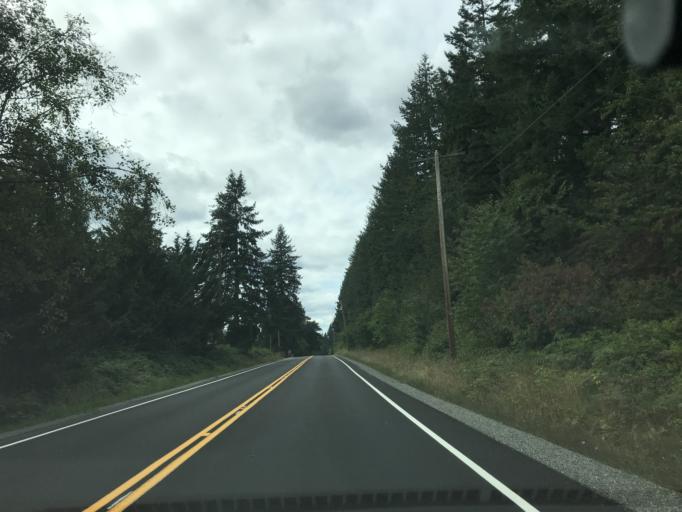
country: US
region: Washington
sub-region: King County
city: Black Diamond
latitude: 47.2867
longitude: -122.0128
